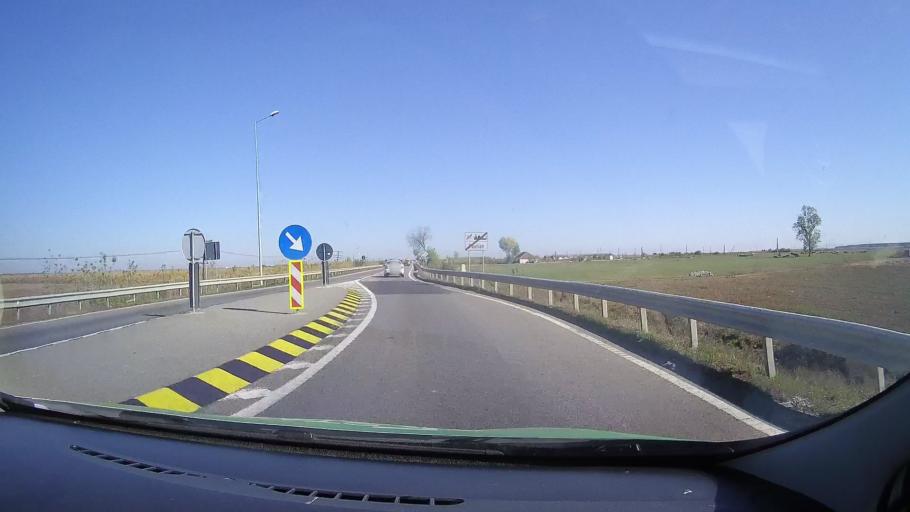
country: RO
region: Satu Mare
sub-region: Comuna Doba
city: Doba
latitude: 47.7322
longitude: 22.6895
